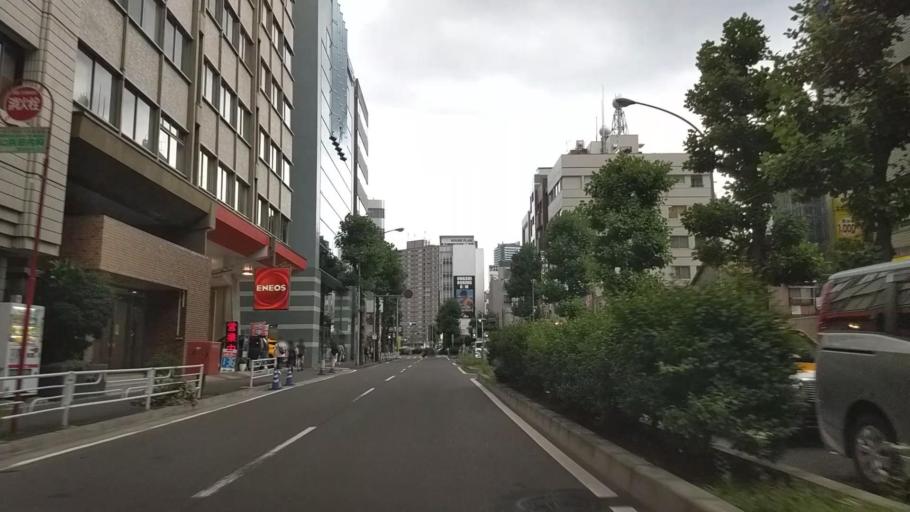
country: JP
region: Kanagawa
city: Yokohama
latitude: 35.4692
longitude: 139.6214
